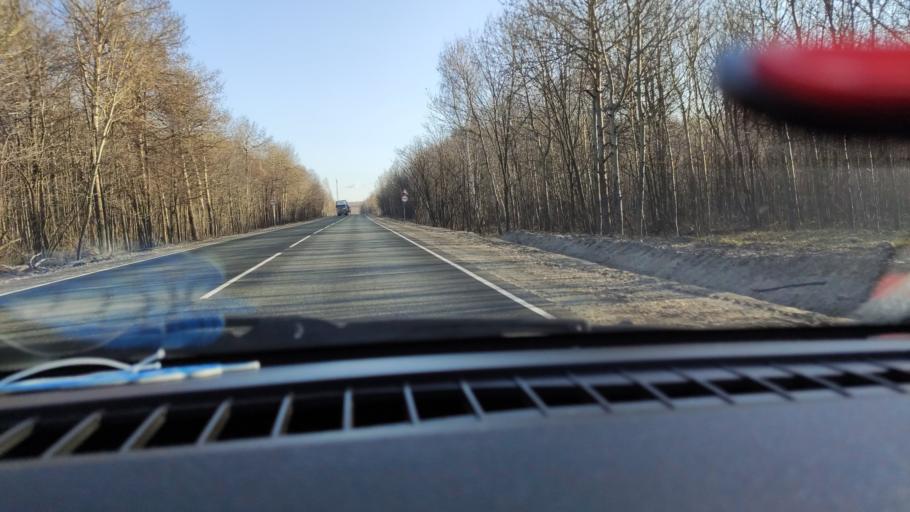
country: RU
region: Saratov
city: Khvalynsk
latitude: 52.4528
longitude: 48.0132
